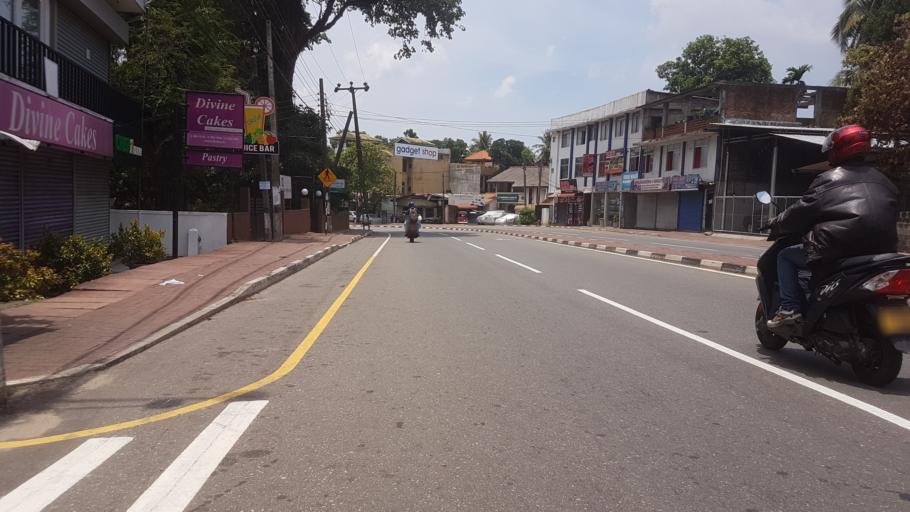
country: LK
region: Western
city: Battaramulla South
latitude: 6.8862
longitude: 79.9321
